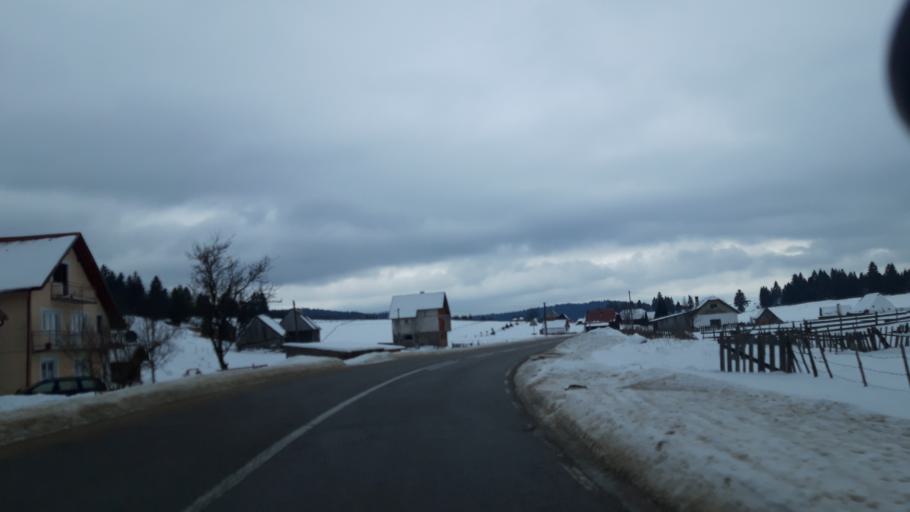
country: BA
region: Republika Srpska
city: Han Pijesak
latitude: 44.1155
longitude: 18.9704
